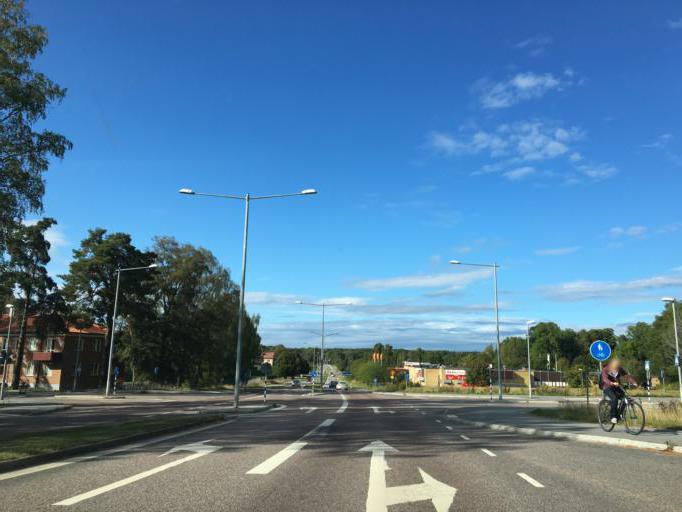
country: SE
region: Soedermanland
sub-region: Nykopings Kommun
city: Nykoping
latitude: 58.7668
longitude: 16.9884
